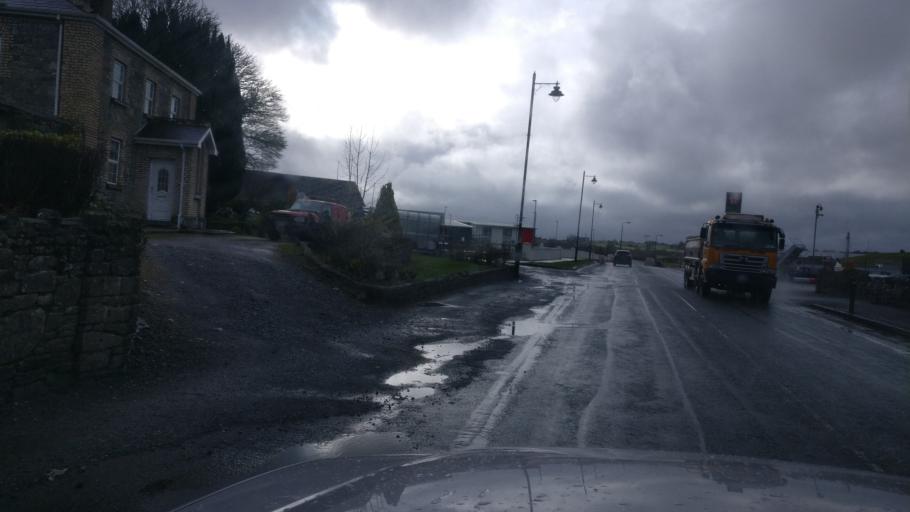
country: IE
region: Leinster
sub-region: An Iarmhi
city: Athlone
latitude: 53.4269
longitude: -8.0198
